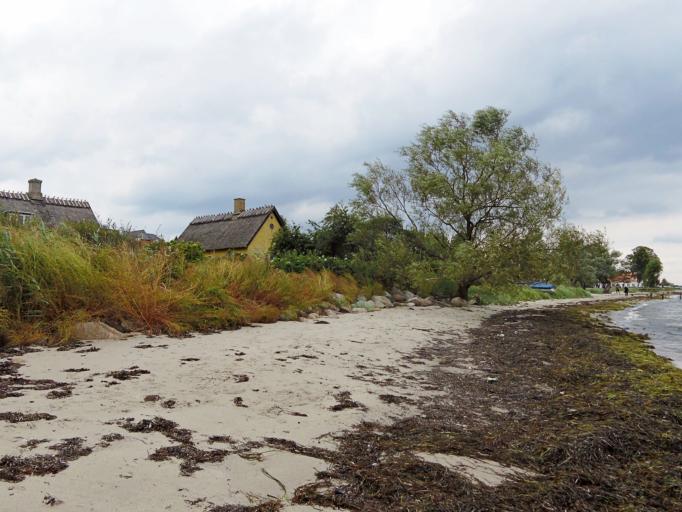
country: DK
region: Capital Region
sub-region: Fredensborg Kommune
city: Humlebaek
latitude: 55.9492
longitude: 12.5314
